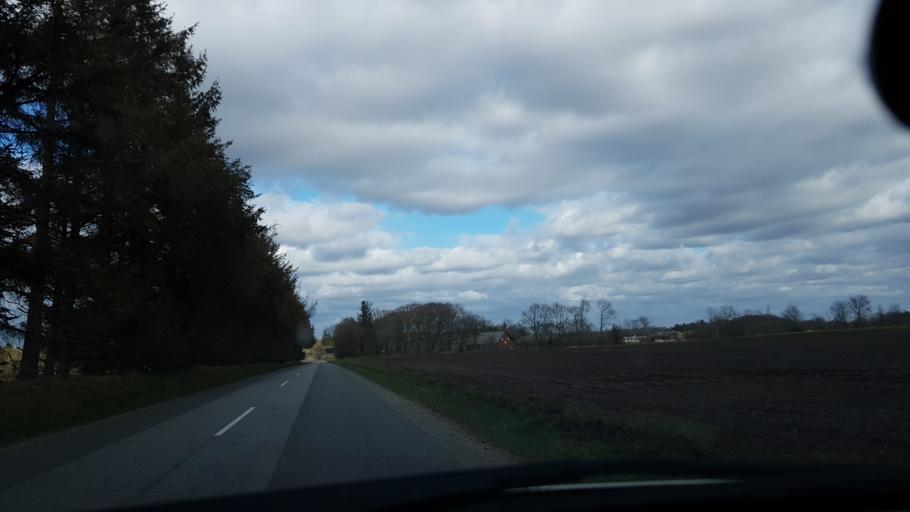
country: DK
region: South Denmark
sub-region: Esbjerg Kommune
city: Ribe
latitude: 55.3108
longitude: 8.8513
